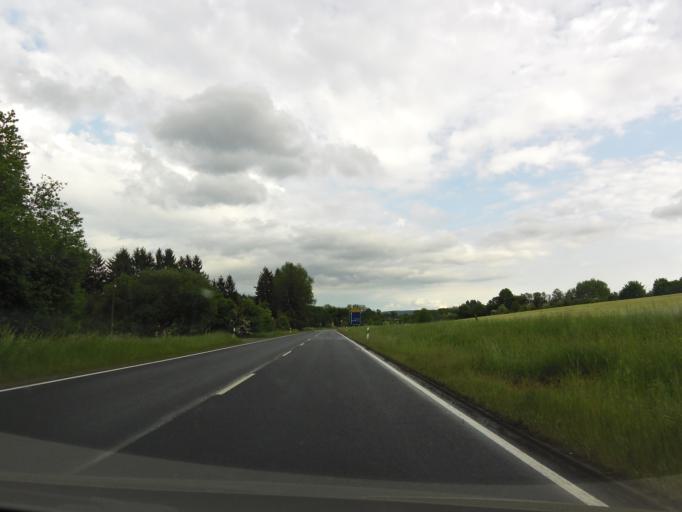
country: DE
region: Thuringia
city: Gerstungen
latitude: 50.9592
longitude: 10.0460
